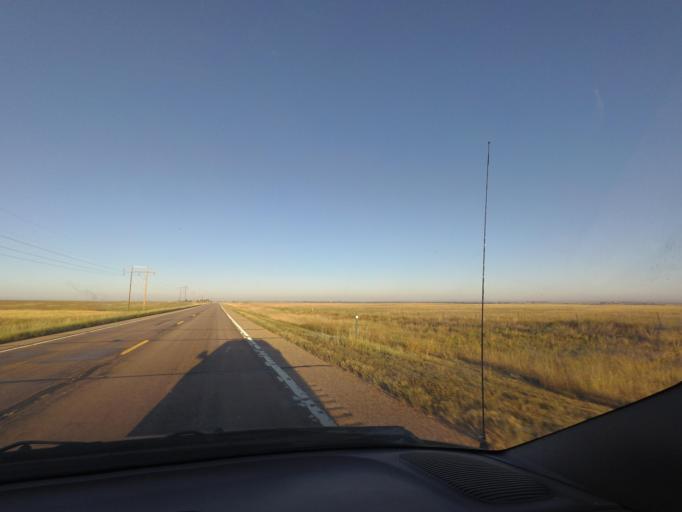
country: US
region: Colorado
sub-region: Yuma County
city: Yuma
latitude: 39.6549
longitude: -102.8057
